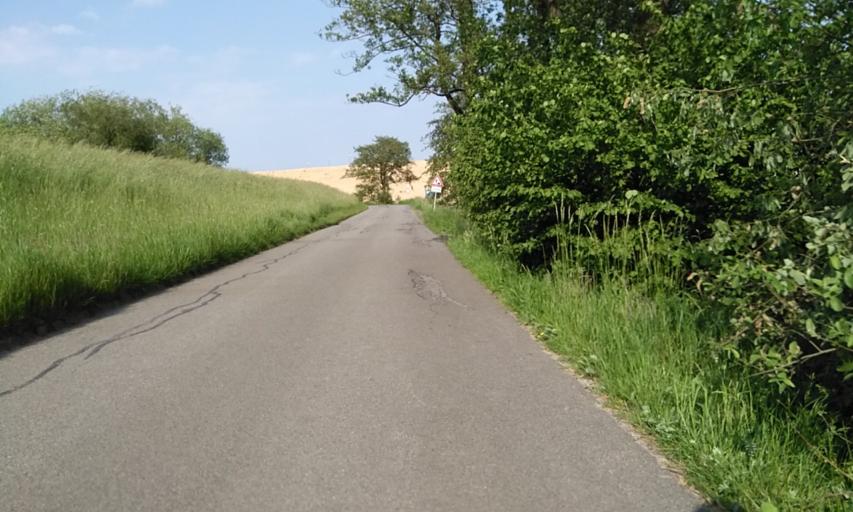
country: DE
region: Lower Saxony
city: Buxtehude
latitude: 53.4862
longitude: 9.7096
